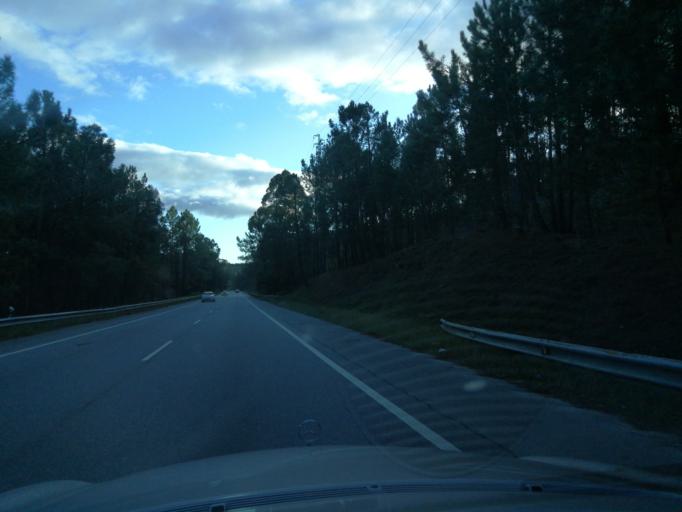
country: PT
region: Braga
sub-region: Barcelos
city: Vila Frescainha
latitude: 41.5523
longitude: -8.6524
